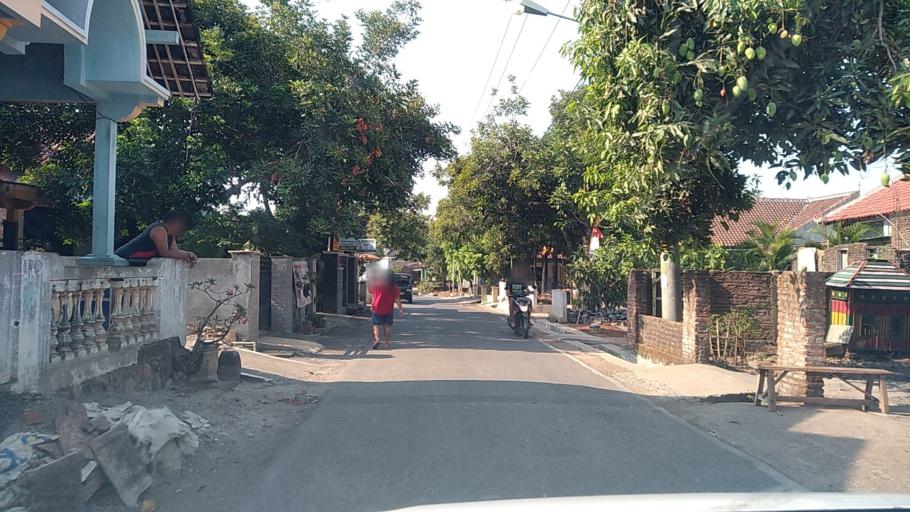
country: ID
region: Central Java
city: Semarang
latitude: -7.0297
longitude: 110.3430
